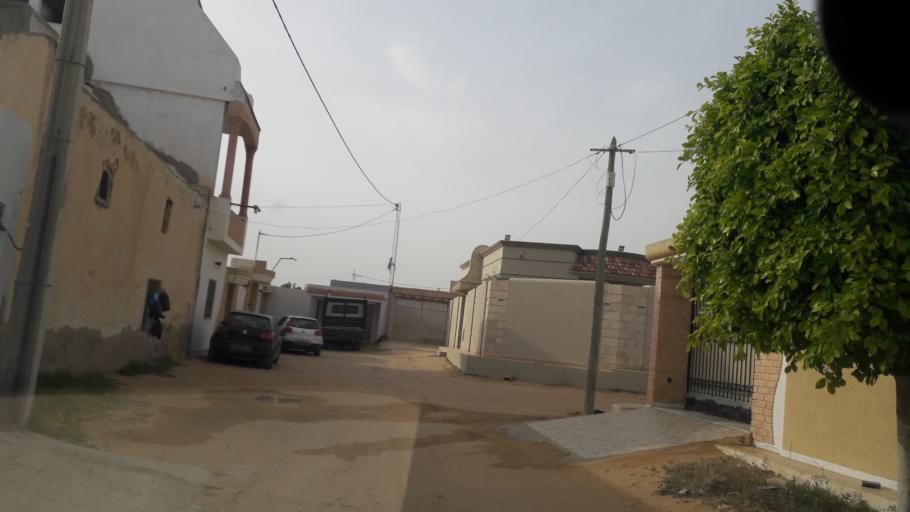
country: TN
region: Safaqis
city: Al Qarmadah
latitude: 34.7814
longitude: 10.7698
